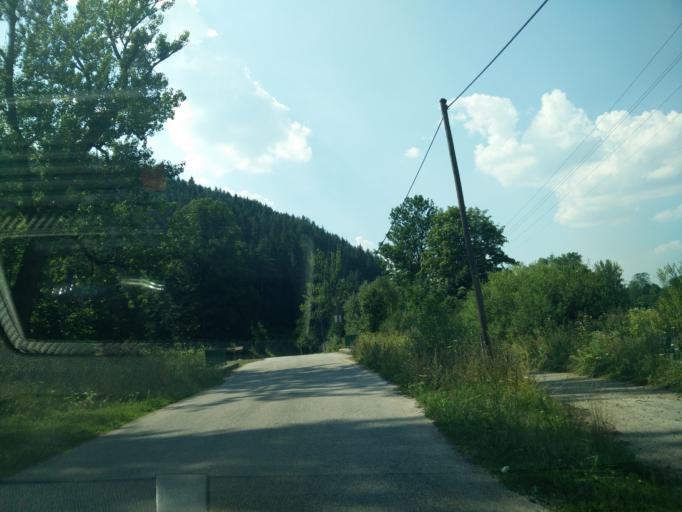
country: SK
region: Zilinsky
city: Rajec
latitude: 49.0384
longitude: 18.6496
